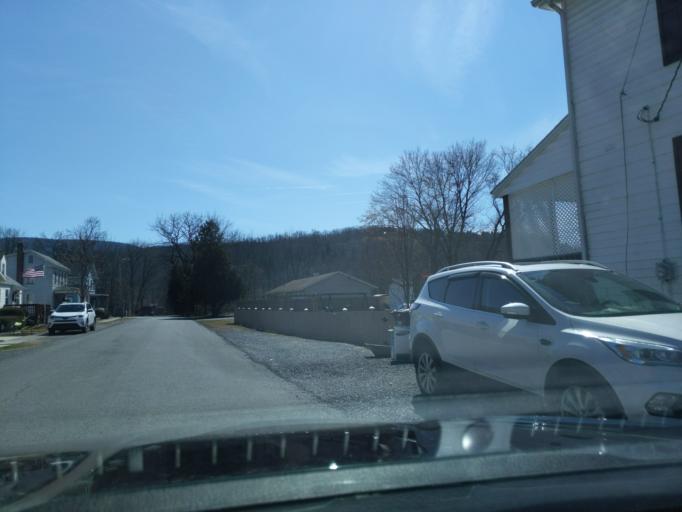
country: US
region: Pennsylvania
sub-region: Blair County
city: Hollidaysburg
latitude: 40.4240
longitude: -78.3961
